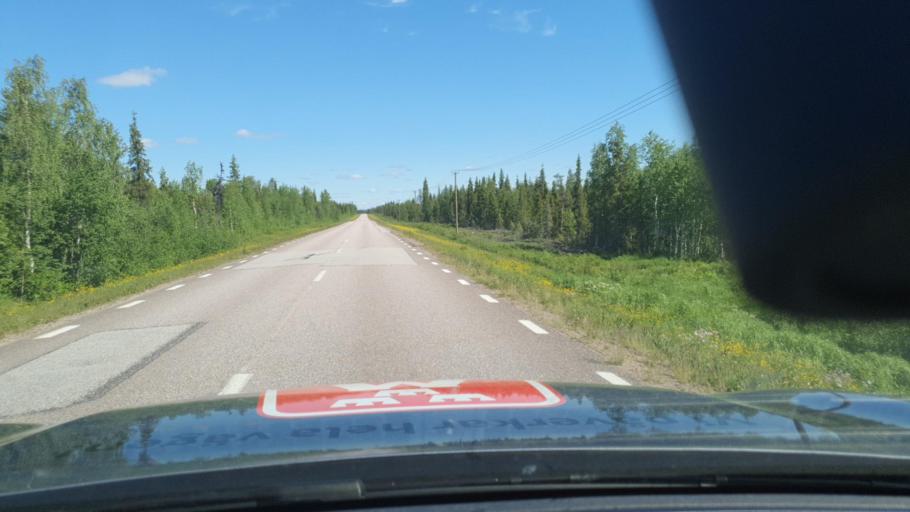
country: SE
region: Norrbotten
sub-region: Overkalix Kommun
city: OEverkalix
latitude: 66.8727
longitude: 22.7595
